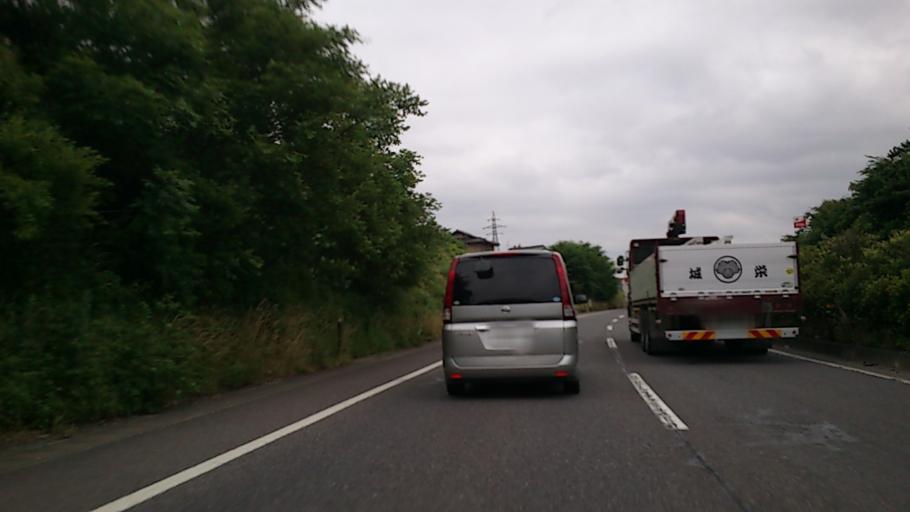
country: JP
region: Fukushima
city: Koriyama
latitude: 37.3777
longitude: 140.3481
